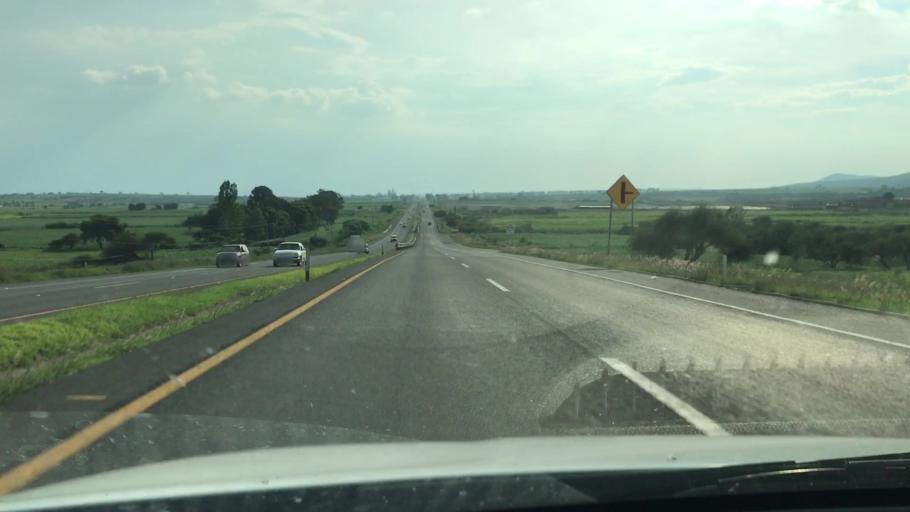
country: MX
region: Guanajuato
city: Penjamo
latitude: 20.3839
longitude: -101.7959
